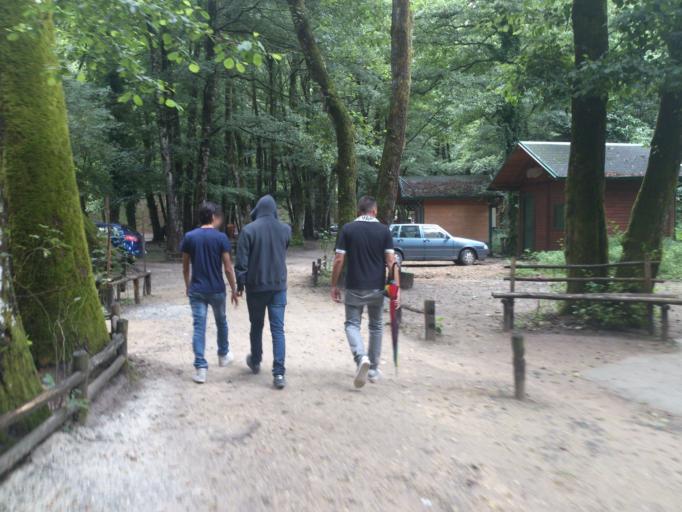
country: IT
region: Calabria
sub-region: Provincia di Vibo-Valentia
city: Serra San Bruno
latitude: 38.5557
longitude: 16.3139
